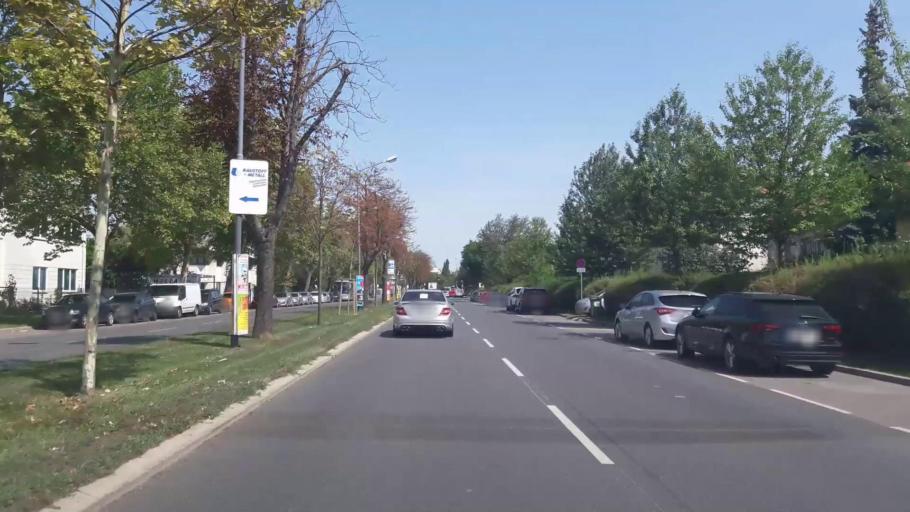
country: AT
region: Lower Austria
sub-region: Politischer Bezirk Modling
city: Vosendorf
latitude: 48.1426
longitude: 16.3602
